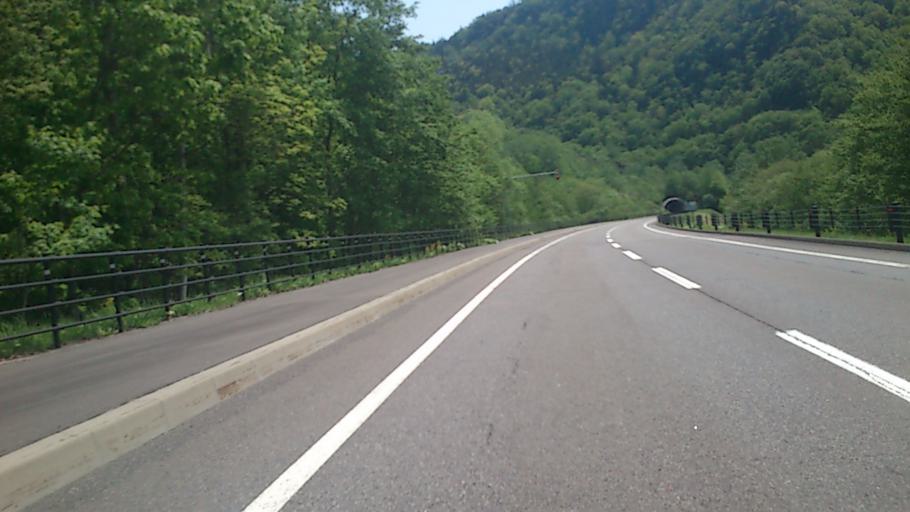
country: JP
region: Hokkaido
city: Otofuke
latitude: 43.3669
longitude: 143.2337
